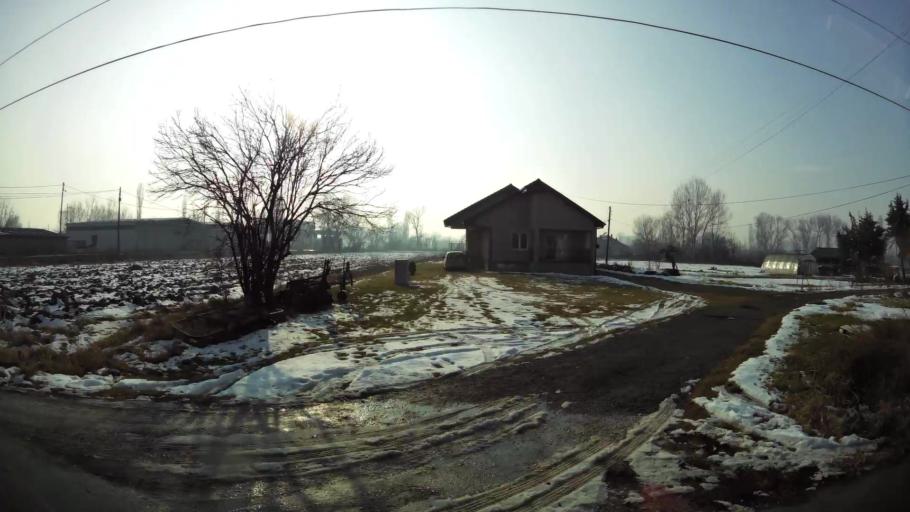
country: MK
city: Kadino
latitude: 41.9633
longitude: 21.5953
